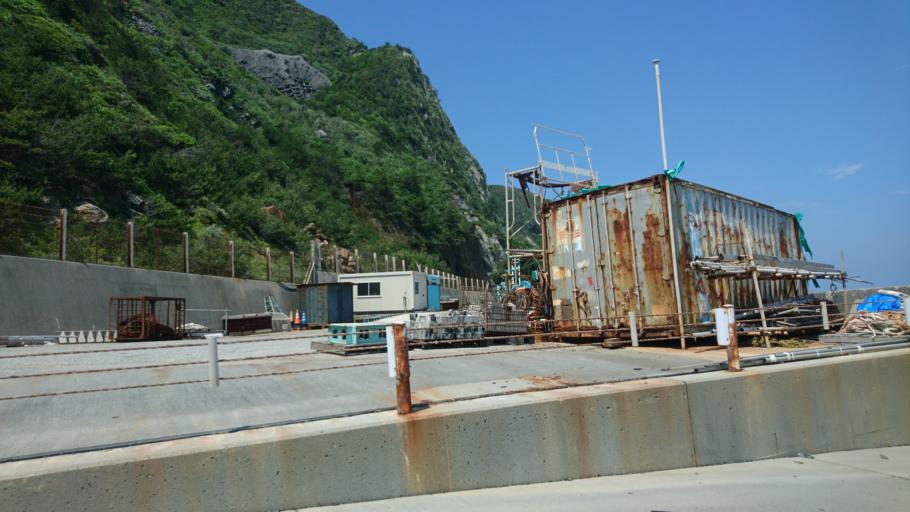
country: JP
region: Shizuoka
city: Shimoda
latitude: 34.3961
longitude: 139.2820
